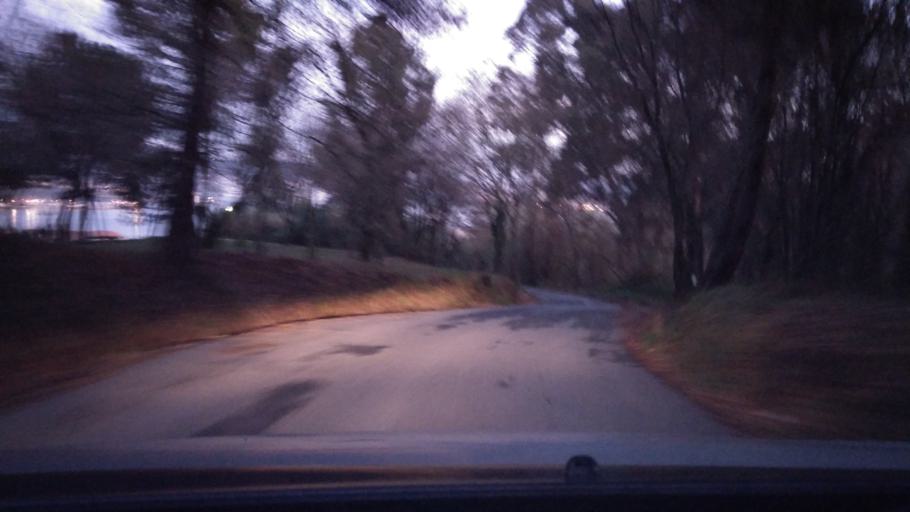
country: ES
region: Galicia
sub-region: Provincia de Pontevedra
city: Moana
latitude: 42.2891
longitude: -8.7375
